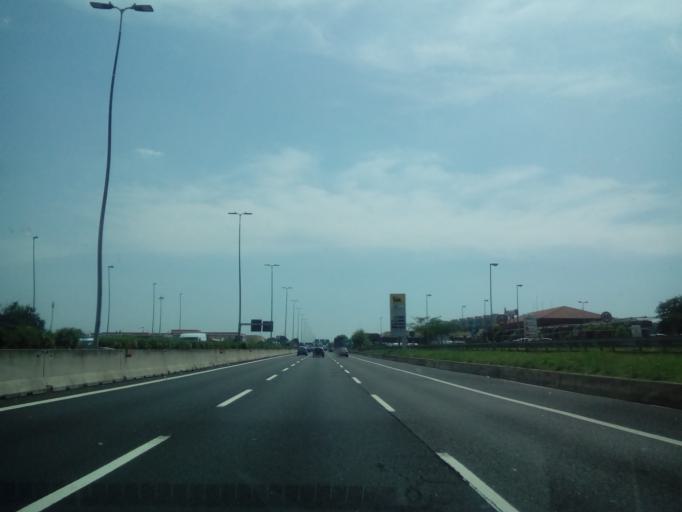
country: IT
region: Latium
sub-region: Citta metropolitana di Roma Capitale
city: Ciampino
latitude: 41.8773
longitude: 12.6081
